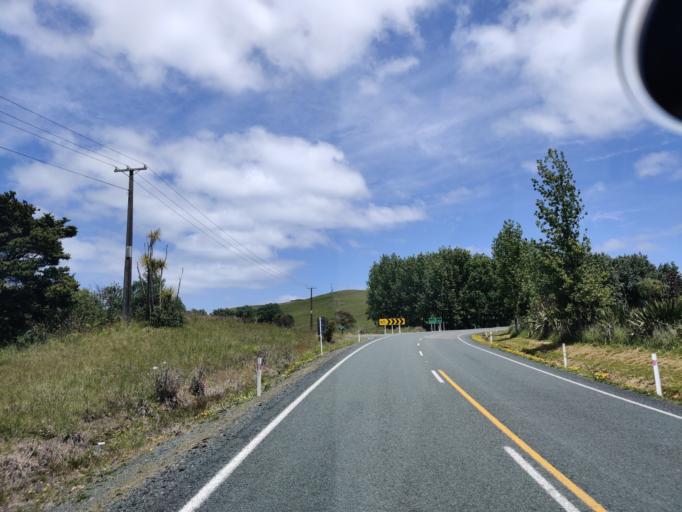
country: NZ
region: Auckland
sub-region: Auckland
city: Wellsford
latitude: -36.3795
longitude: 174.4509
